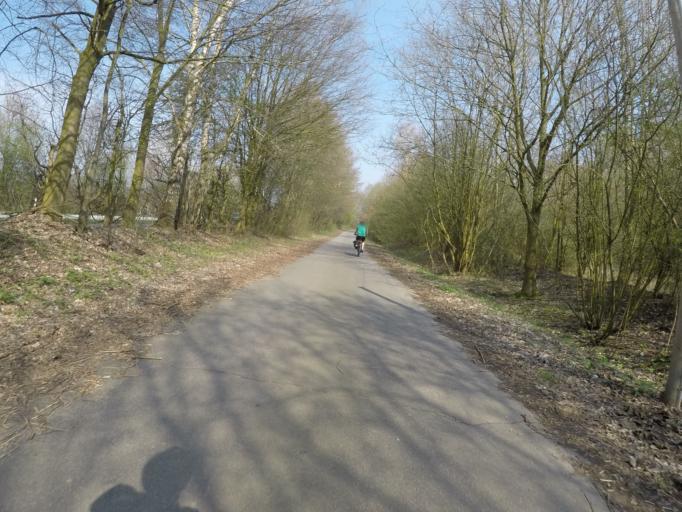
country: DE
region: Schleswig-Holstein
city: Tangstedt
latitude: 53.7264
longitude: 10.0977
